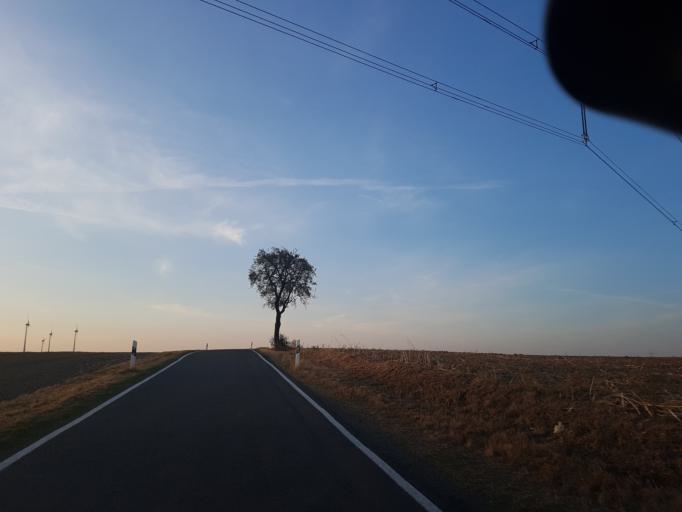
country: DE
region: Saxony
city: Stauchitz
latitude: 51.3006
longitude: 13.1884
